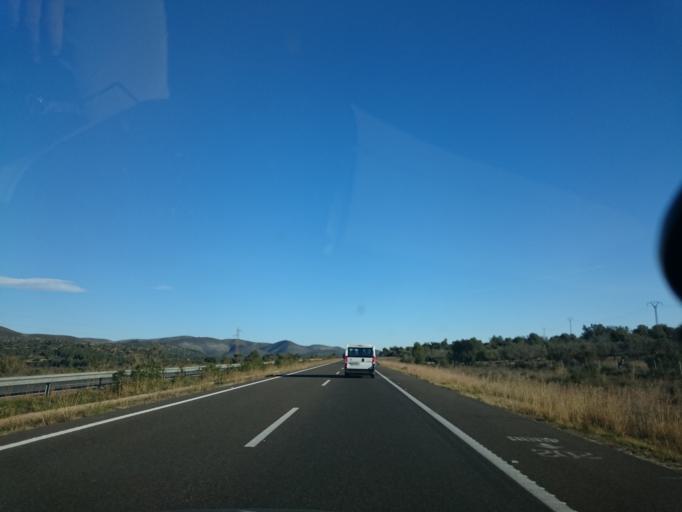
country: ES
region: Valencia
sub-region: Provincia de Castello
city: Santa Magdalena de Pulpis
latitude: 40.3358
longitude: 0.2667
